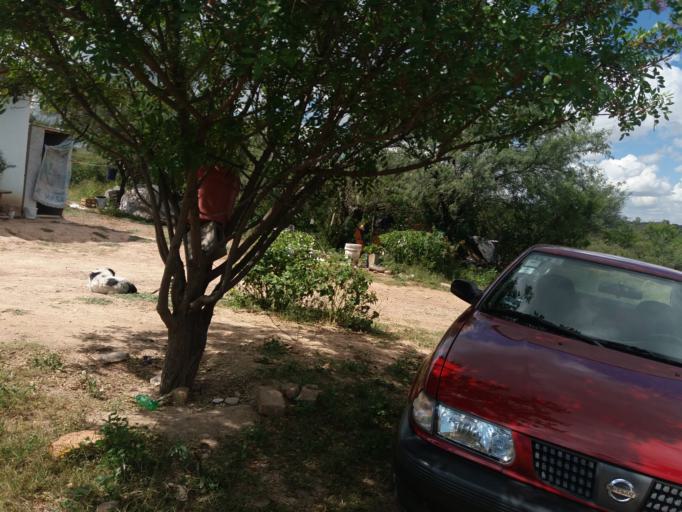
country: MX
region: Aguascalientes
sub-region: Aguascalientes
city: San Sebastian [Fraccionamiento]
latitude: 21.8050
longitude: -102.2436
